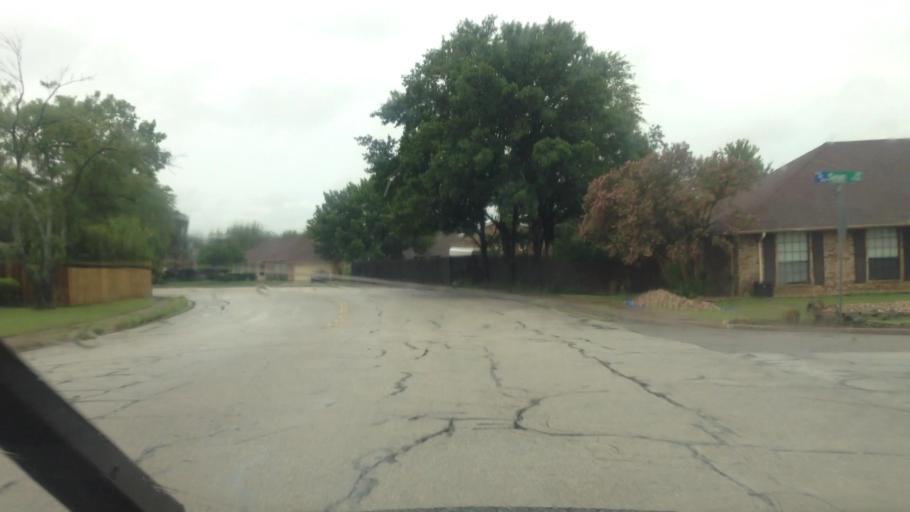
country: US
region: Texas
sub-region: Tarrant County
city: North Richland Hills
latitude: 32.8660
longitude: -97.2194
